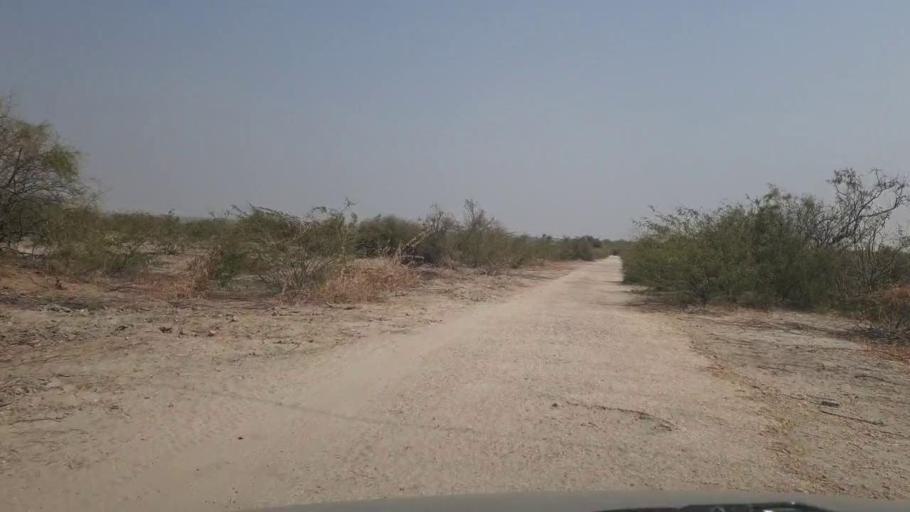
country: PK
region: Sindh
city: Chor
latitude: 25.4528
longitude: 69.7905
